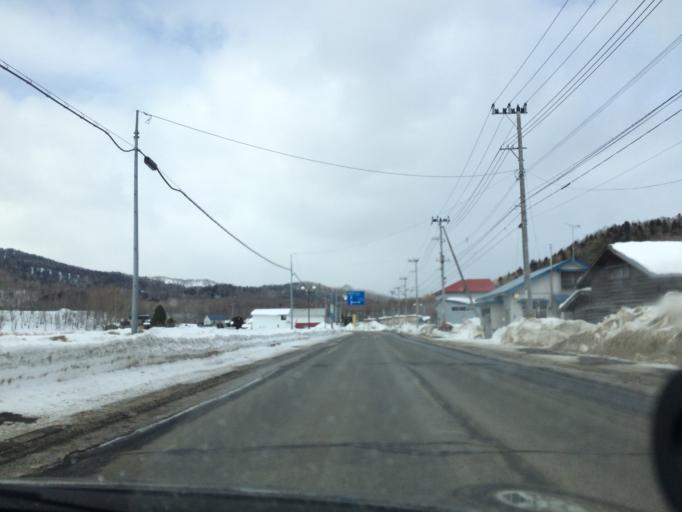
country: JP
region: Hokkaido
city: Shimo-furano
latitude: 43.0039
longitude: 142.4067
